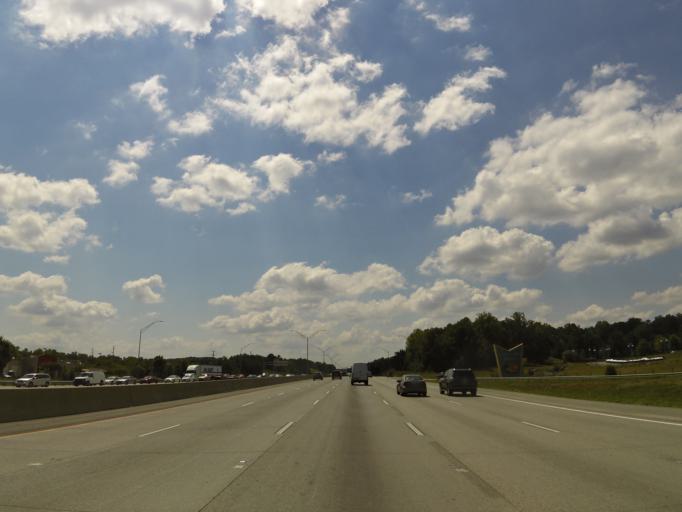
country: US
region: North Carolina
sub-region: Cabarrus County
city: Harrisburg
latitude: 35.3670
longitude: -80.7156
